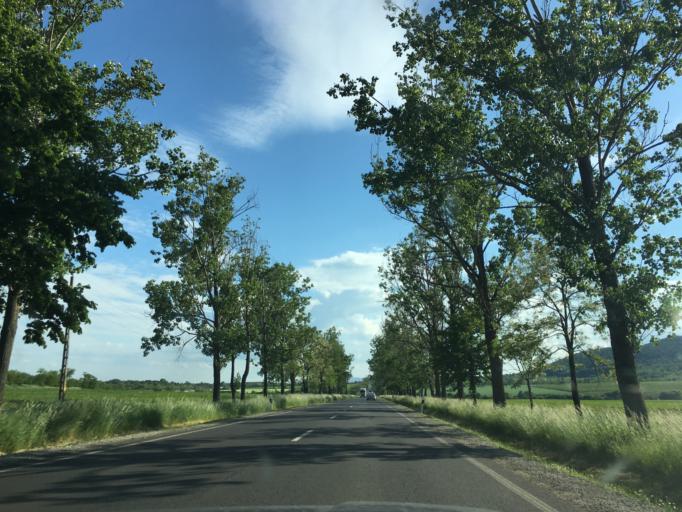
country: HU
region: Borsod-Abauj-Zemplen
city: Sarospatak
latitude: 48.3017
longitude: 21.5188
